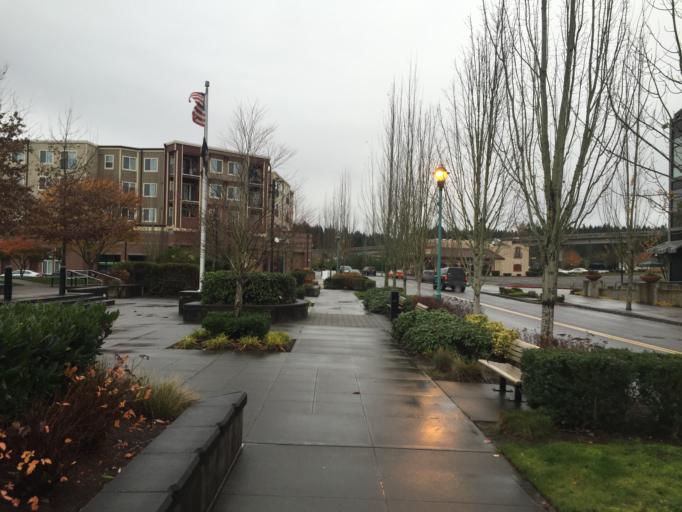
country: US
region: Washington
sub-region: Pierce County
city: DuPont
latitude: 47.0912
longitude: -122.6435
